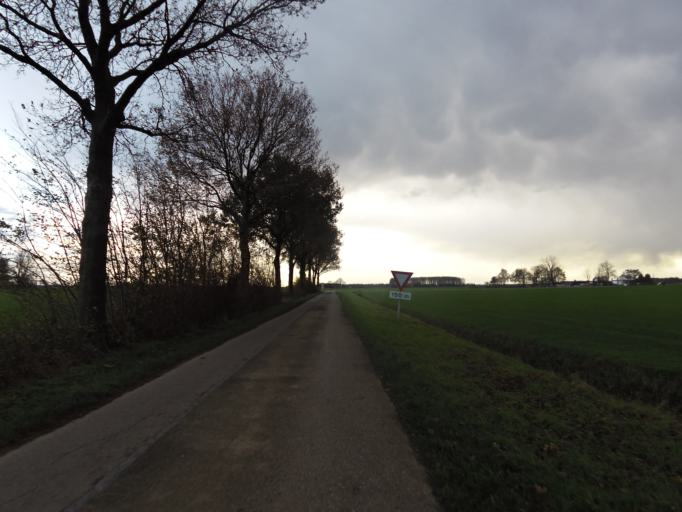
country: NL
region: Gelderland
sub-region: Gemeente Montferland
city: s-Heerenberg
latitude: 51.8755
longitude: 6.2921
